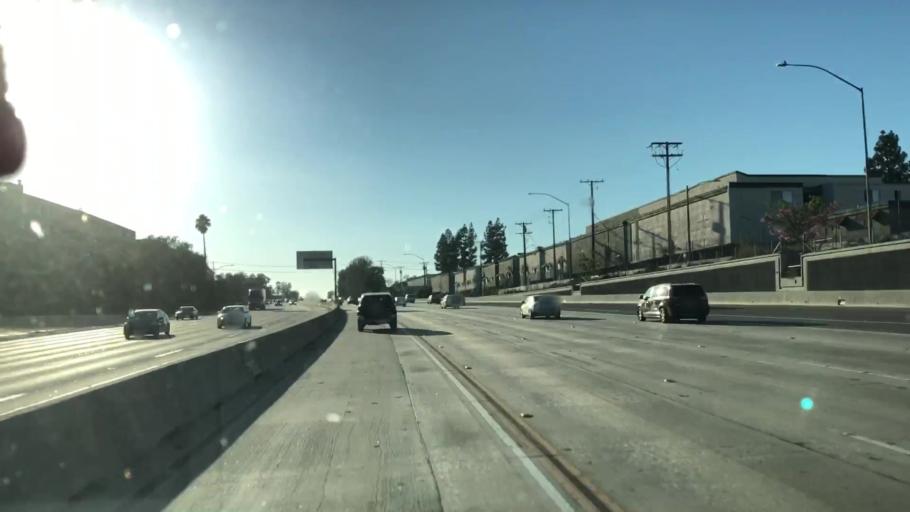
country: US
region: California
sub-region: Los Angeles County
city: Universal City
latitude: 34.1541
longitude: -118.3466
